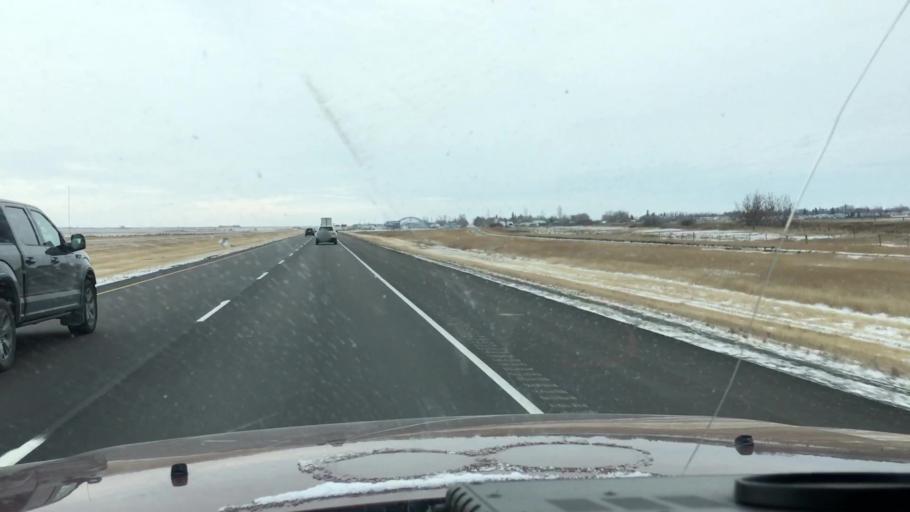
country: CA
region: Saskatchewan
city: Saskatoon
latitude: 51.8229
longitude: -106.5000
